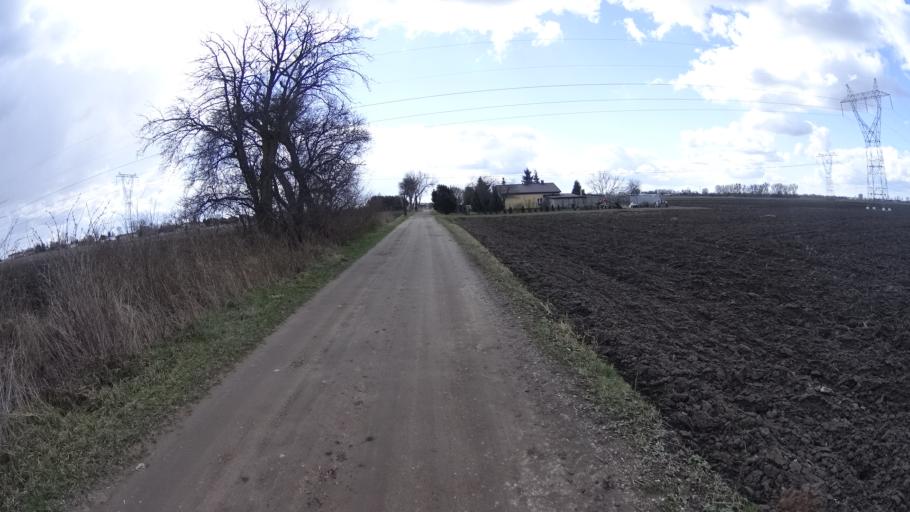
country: PL
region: Masovian Voivodeship
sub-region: Powiat warszawski zachodni
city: Jozefow
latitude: 52.2279
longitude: 20.7257
